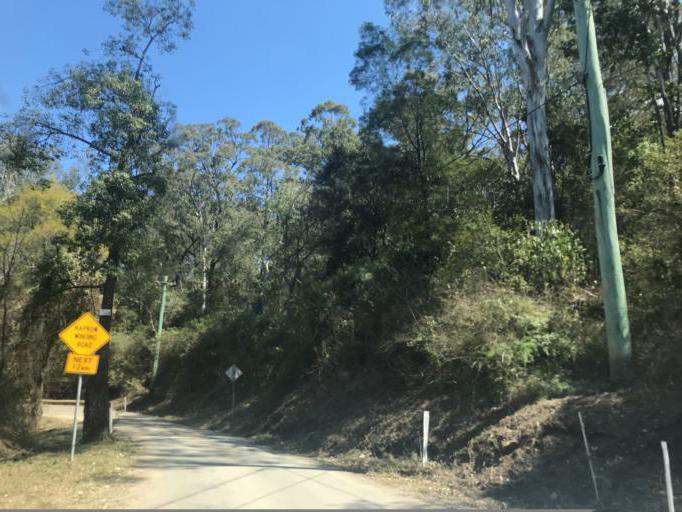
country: AU
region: New South Wales
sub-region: Hawkesbury
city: Pitt Town
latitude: -33.4147
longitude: 150.9163
